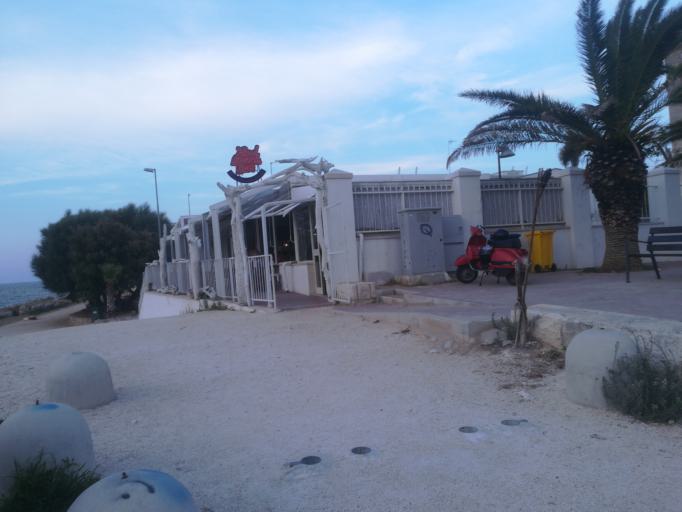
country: IT
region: Apulia
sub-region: Provincia di Bari
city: Monopoli
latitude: 40.9462
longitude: 17.3080
